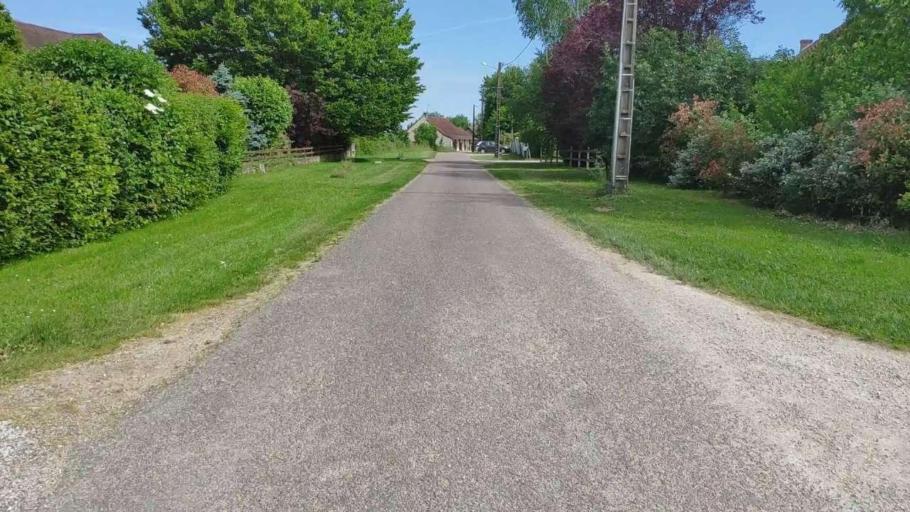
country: FR
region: Franche-Comte
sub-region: Departement du Jura
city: Bletterans
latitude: 46.7115
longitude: 5.4449
